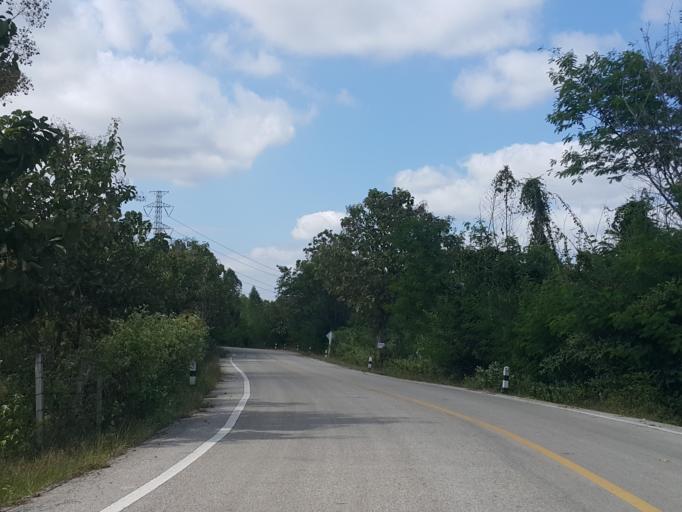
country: TH
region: Lamphun
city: Mae Tha
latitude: 18.5298
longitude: 99.0818
